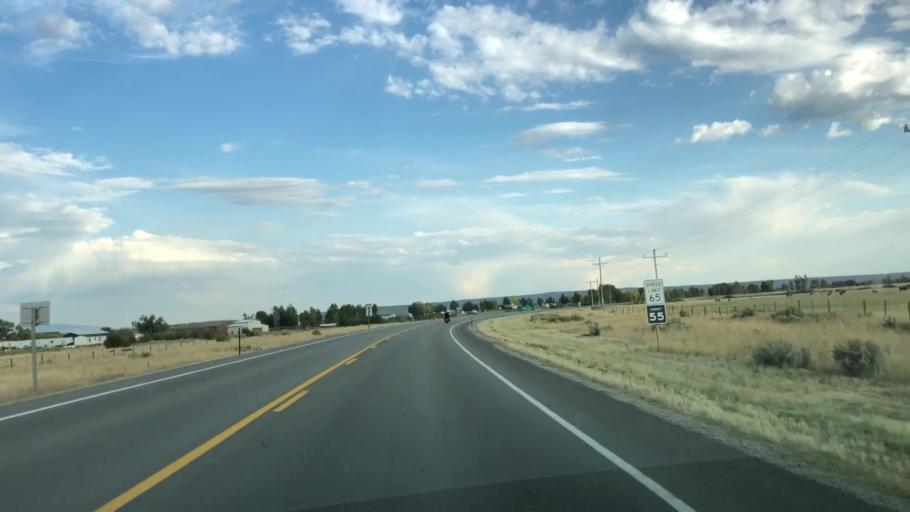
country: US
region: Wyoming
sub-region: Sublette County
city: Pinedale
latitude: 42.7446
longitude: -109.7196
